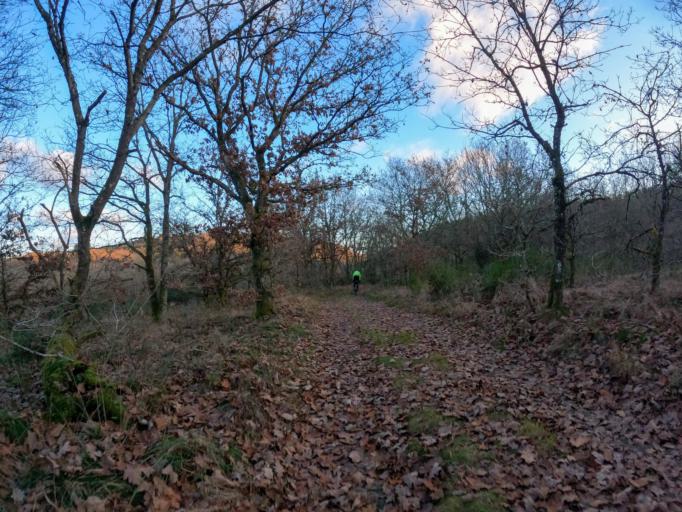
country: LU
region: Diekirch
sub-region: Canton de Wiltz
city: Bavigne
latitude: 49.9148
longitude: 5.8559
